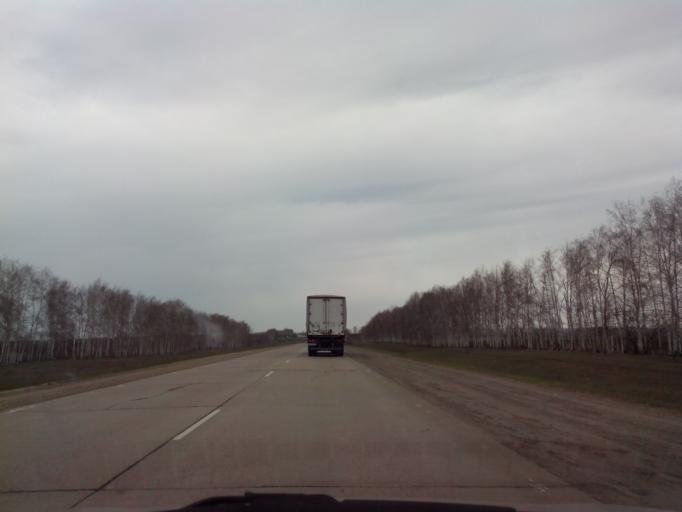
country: RU
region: Tambov
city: Pokrovo-Prigorodnoye
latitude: 52.6510
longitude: 41.3407
